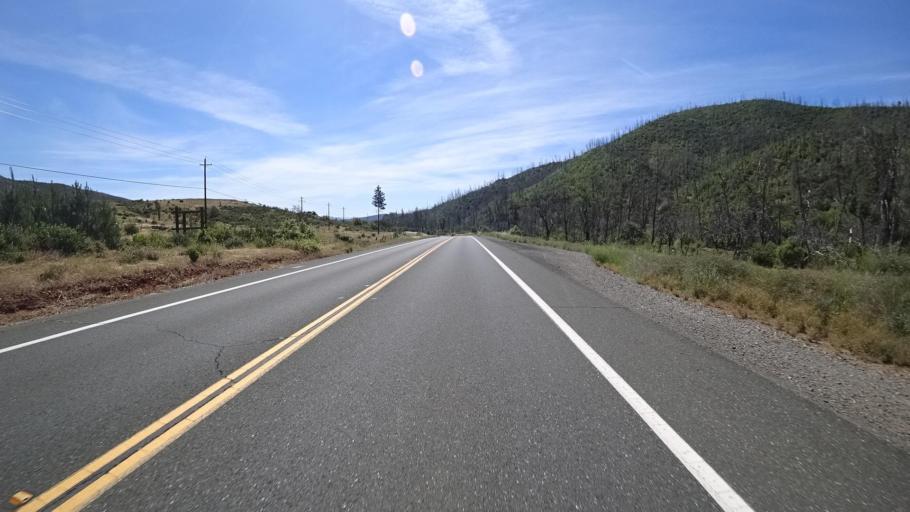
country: US
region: California
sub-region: Lake County
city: Middletown
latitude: 38.7762
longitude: -122.6761
